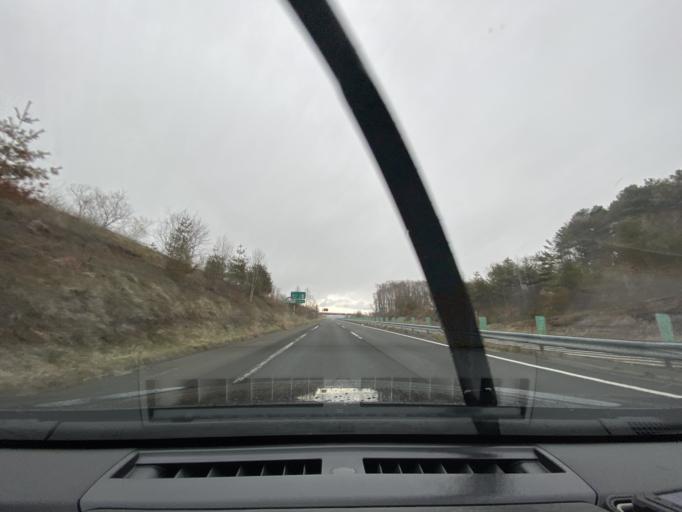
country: JP
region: Hokkaido
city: Chitose
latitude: 42.8932
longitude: 141.8060
